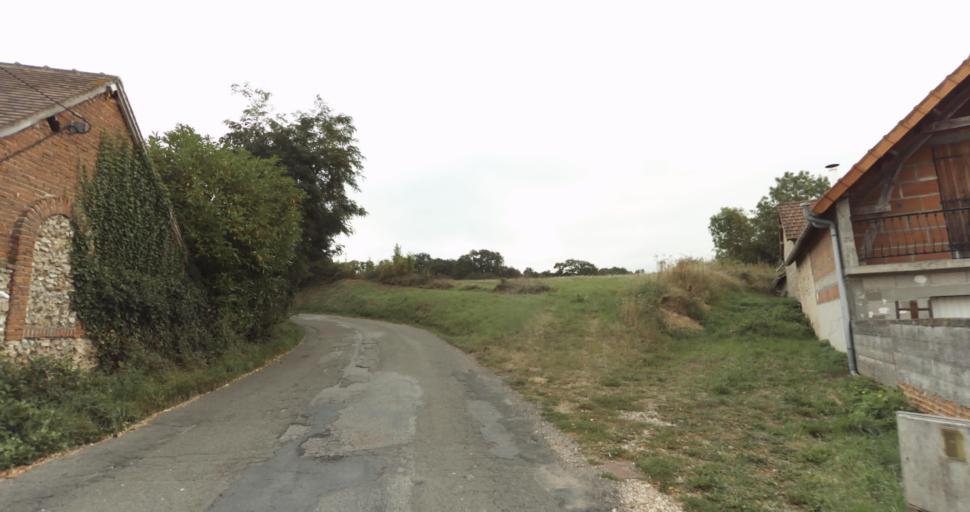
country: FR
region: Haute-Normandie
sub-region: Departement de l'Eure
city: Saint-Germain-sur-Avre
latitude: 48.7667
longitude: 1.2635
